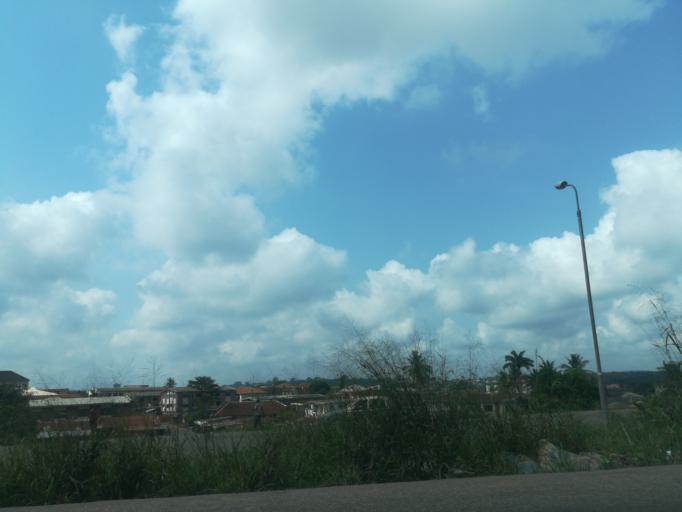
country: NG
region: Oyo
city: Moniya
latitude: 7.4592
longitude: 3.9183
